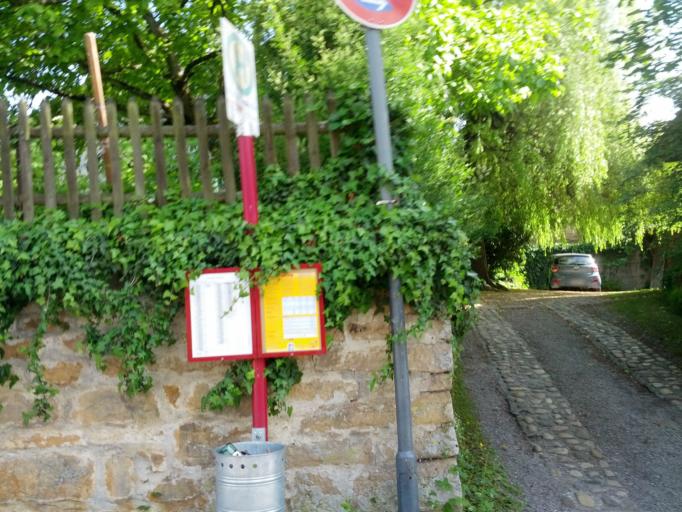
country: DE
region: Baden-Wuerttemberg
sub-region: Freiburg Region
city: Ebringen
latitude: 47.9579
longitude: 7.7773
